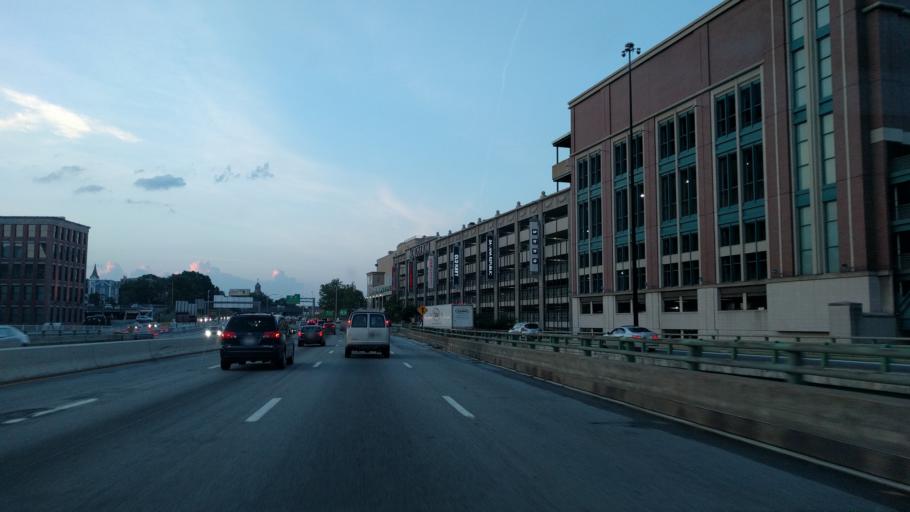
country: US
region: Rhode Island
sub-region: Providence County
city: Providence
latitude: 41.8275
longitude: -71.4182
